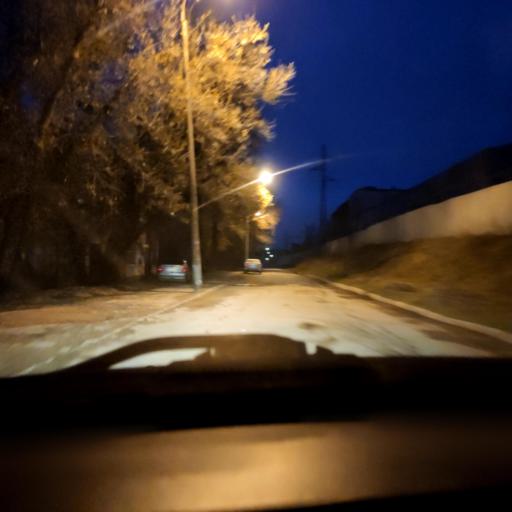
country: RU
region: Samara
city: Volzhskiy
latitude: 53.3450
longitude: 50.2089
